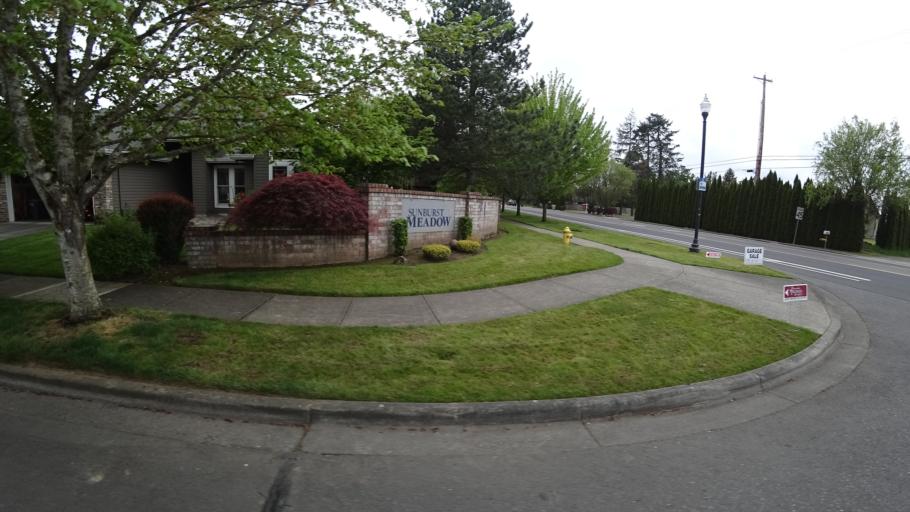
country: US
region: Oregon
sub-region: Washington County
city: Hillsboro
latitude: 45.5498
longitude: -122.9863
